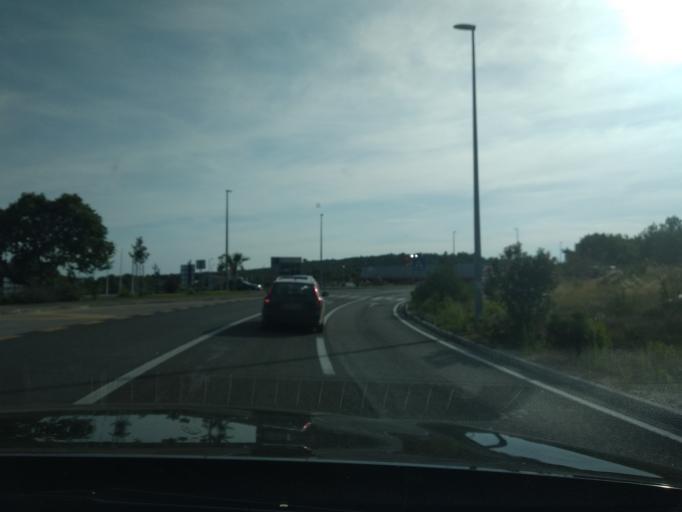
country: HR
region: Sibensko-Kniniska
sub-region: Grad Sibenik
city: Tisno
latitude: 43.7900
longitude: 15.6324
